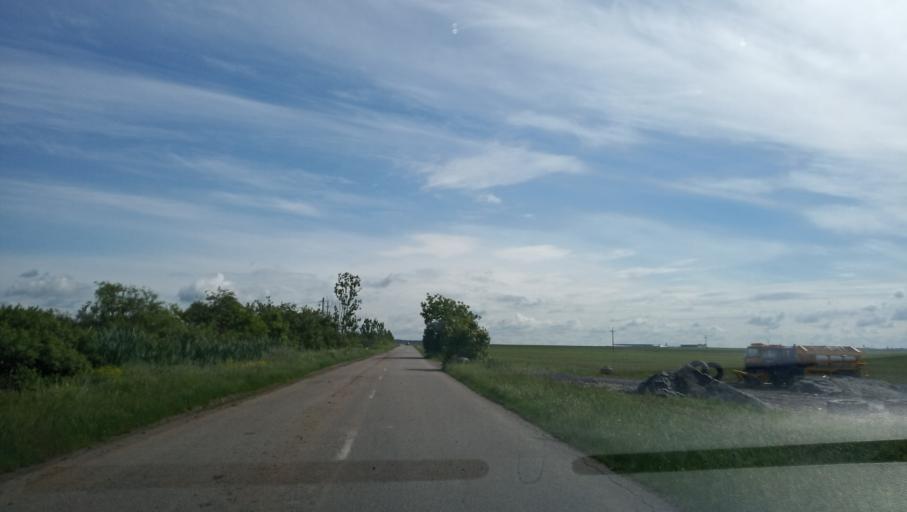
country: RO
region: Timis
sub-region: Comuna Topolovatu Mare
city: Topolovatu Mare
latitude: 45.7774
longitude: 21.6329
